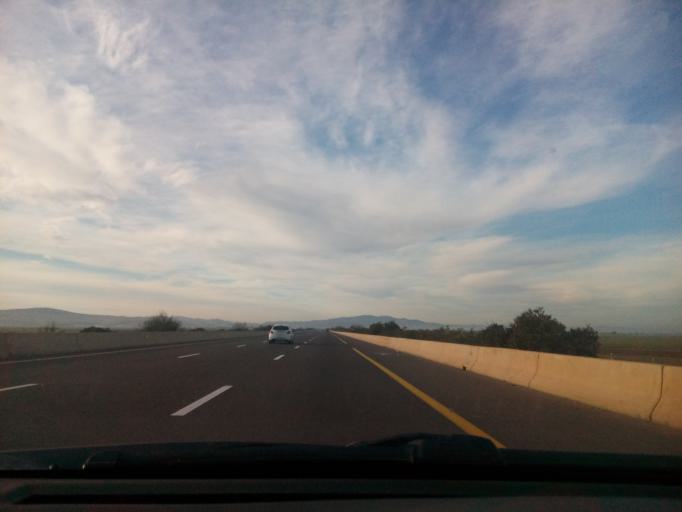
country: DZ
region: Mostaganem
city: Mostaganem
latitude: 35.6692
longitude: 0.1430
